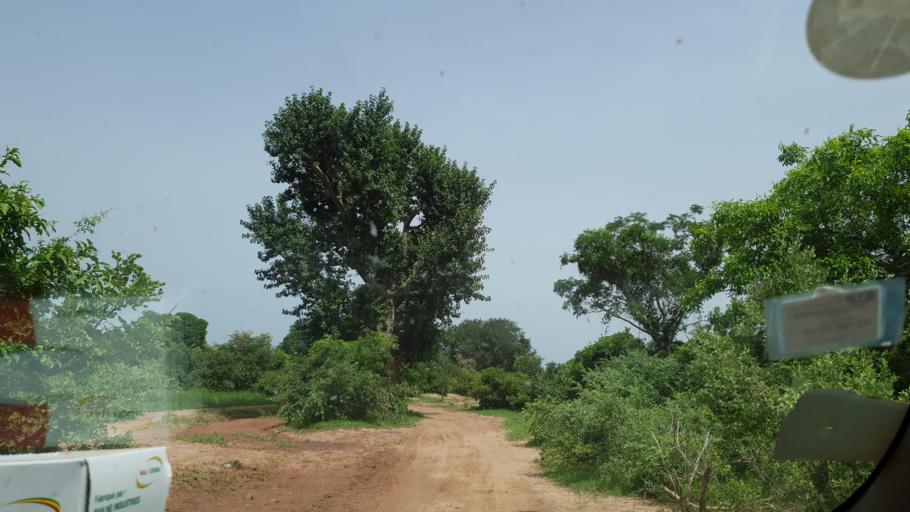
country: ML
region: Koulikoro
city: Koulikoro
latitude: 12.6681
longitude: -7.2424
